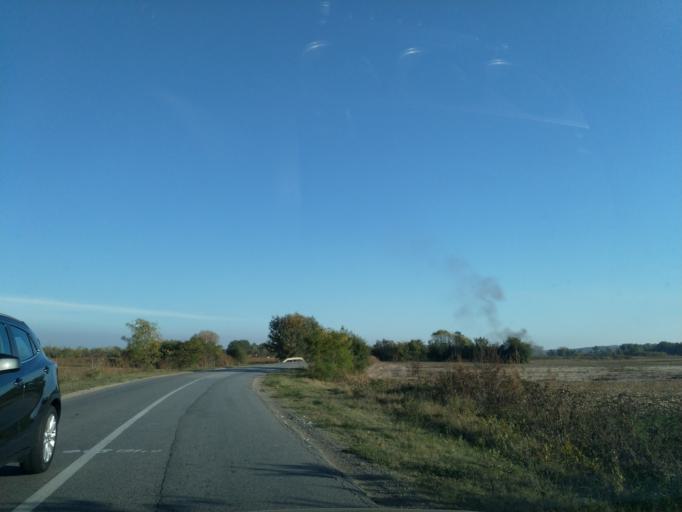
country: RS
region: Central Serbia
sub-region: Pomoravski Okrug
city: Svilajnac
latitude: 44.2367
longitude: 21.1359
